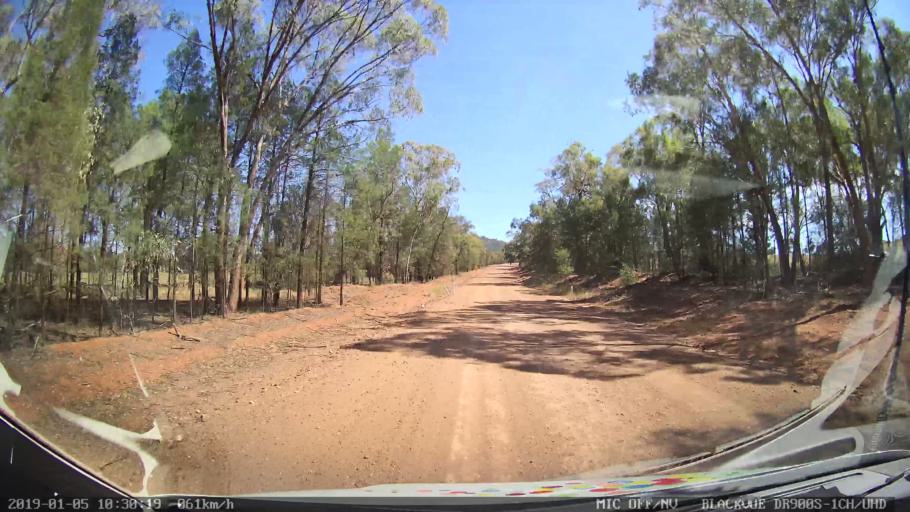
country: AU
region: New South Wales
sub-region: Gilgandra
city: Gilgandra
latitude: -31.5335
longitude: 148.9249
